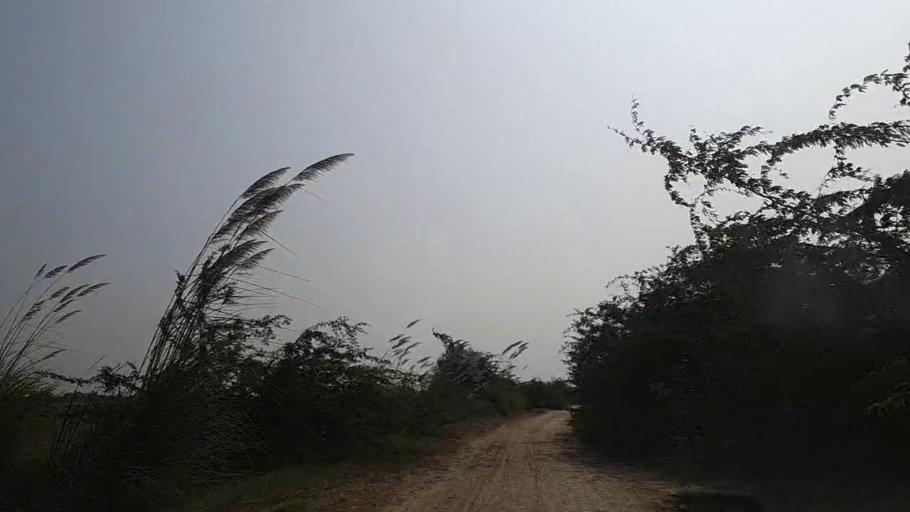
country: PK
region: Sindh
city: Mirpur Sakro
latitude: 24.5978
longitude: 67.7163
